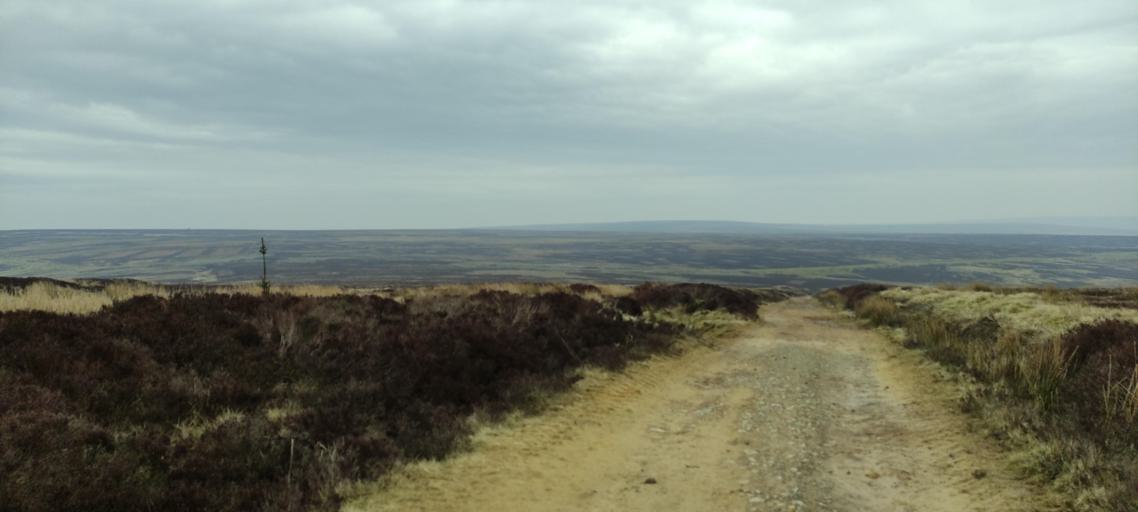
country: GB
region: England
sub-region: North Yorkshire
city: Ingleby Greenhow
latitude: 54.4061
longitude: -1.0683
